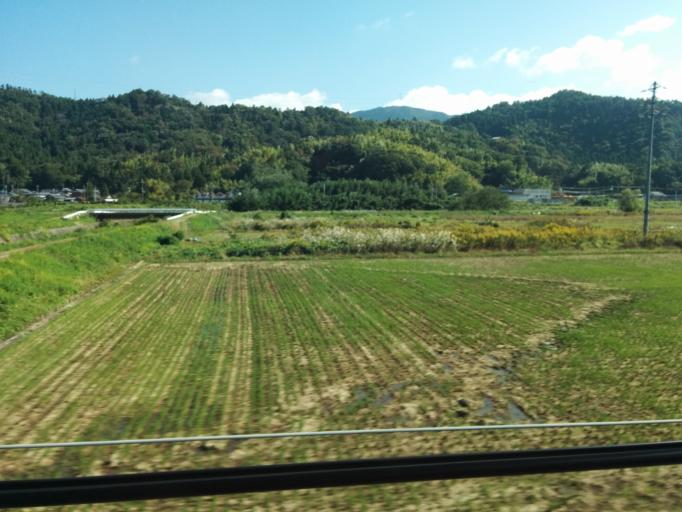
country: JP
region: Shiga Prefecture
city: Hikone
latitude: 35.2980
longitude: 136.2830
